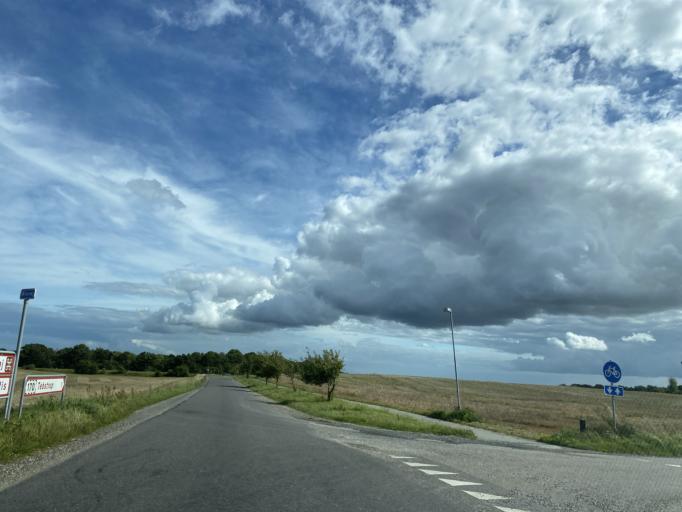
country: DK
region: Central Jutland
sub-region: Skanderborg Kommune
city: Skanderborg
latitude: 55.9766
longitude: 9.8556
